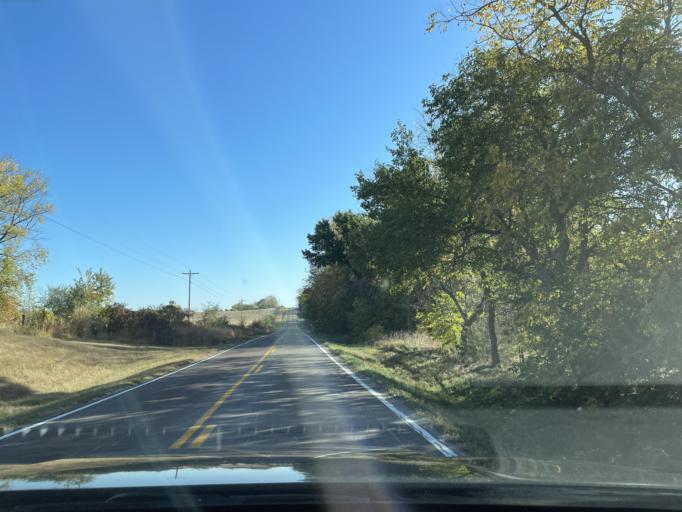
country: US
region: Missouri
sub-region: Andrew County
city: Savannah
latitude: 39.9180
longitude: -94.8718
